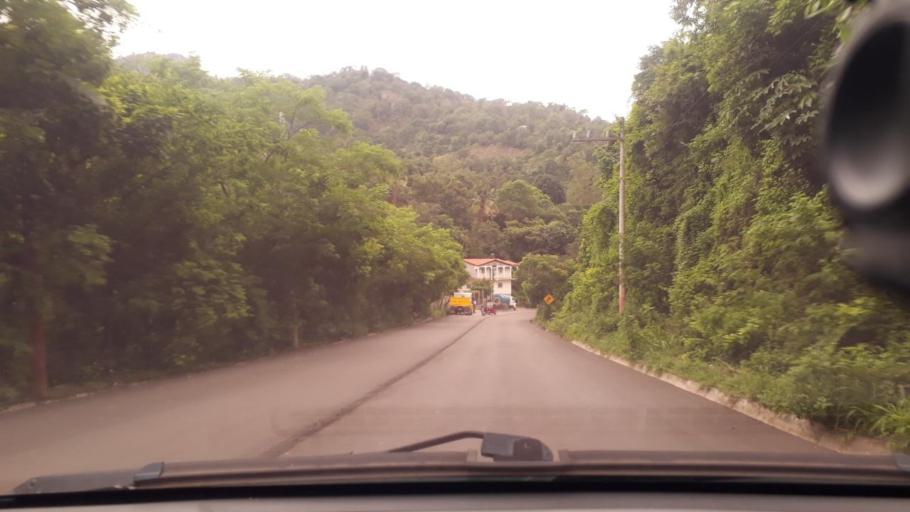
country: GT
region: Chiquimula
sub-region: Municipio de San Juan Ermita
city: San Juan Ermita
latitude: 14.7611
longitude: -89.4376
